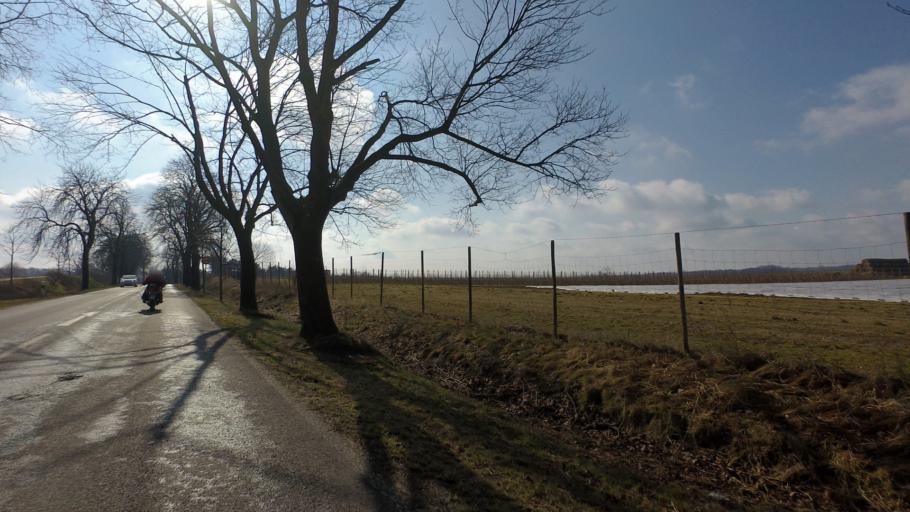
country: DE
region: Brandenburg
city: Glienicke
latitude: 52.6573
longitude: 13.3339
